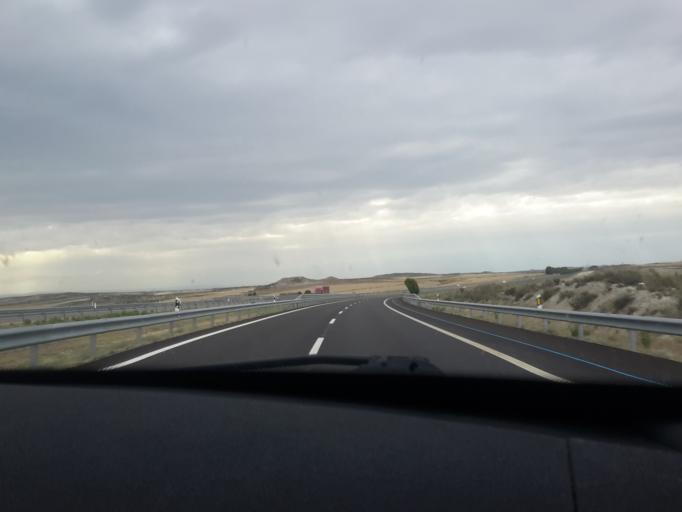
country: ES
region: Aragon
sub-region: Provincia de Huesca
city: Castejon de Monegros
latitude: 41.5181
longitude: -0.3063
